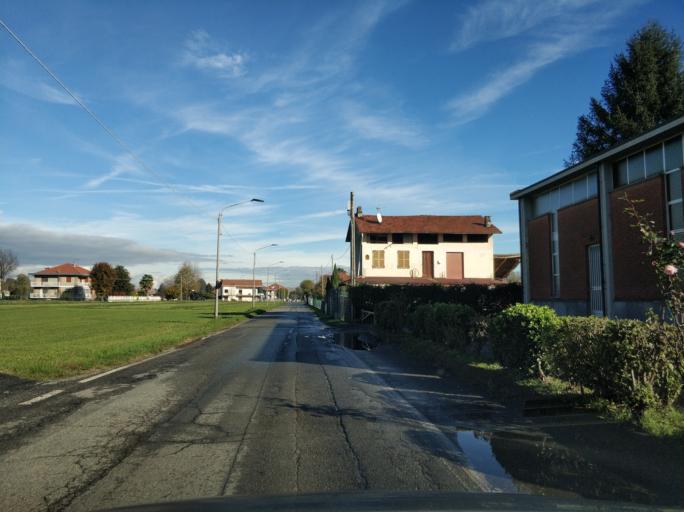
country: IT
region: Piedmont
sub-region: Provincia di Torino
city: Cirie
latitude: 45.2259
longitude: 7.5835
